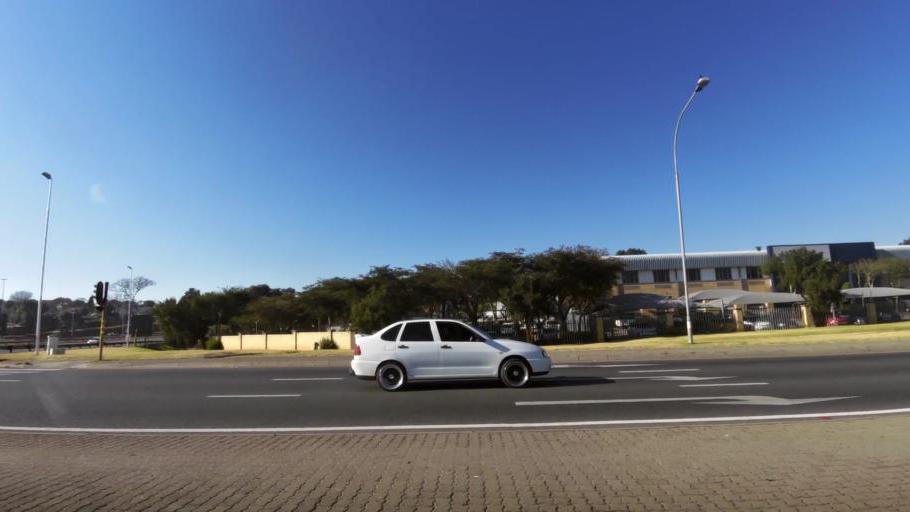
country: ZA
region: Gauteng
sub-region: City of Johannesburg Metropolitan Municipality
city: Roodepoort
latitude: -26.1667
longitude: 27.9392
